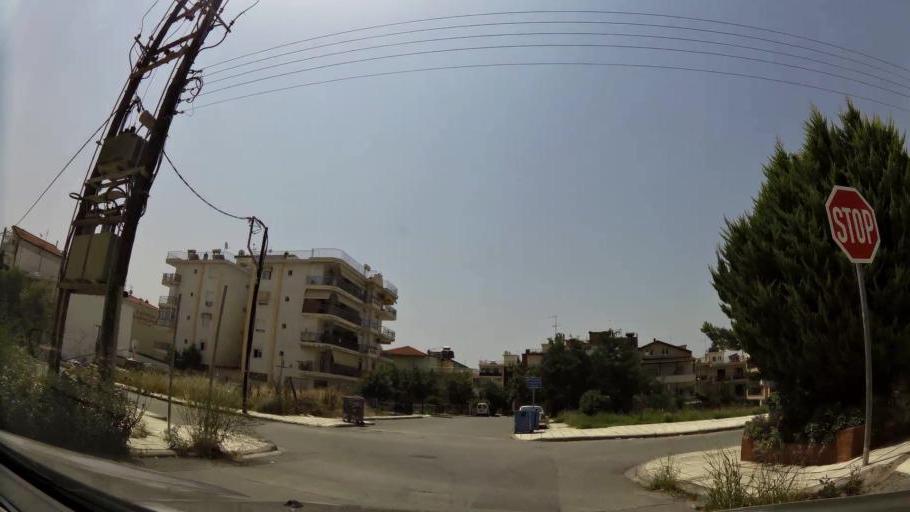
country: GR
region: Central Macedonia
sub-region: Nomos Thessalonikis
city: Evosmos
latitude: 40.6764
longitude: 22.8984
